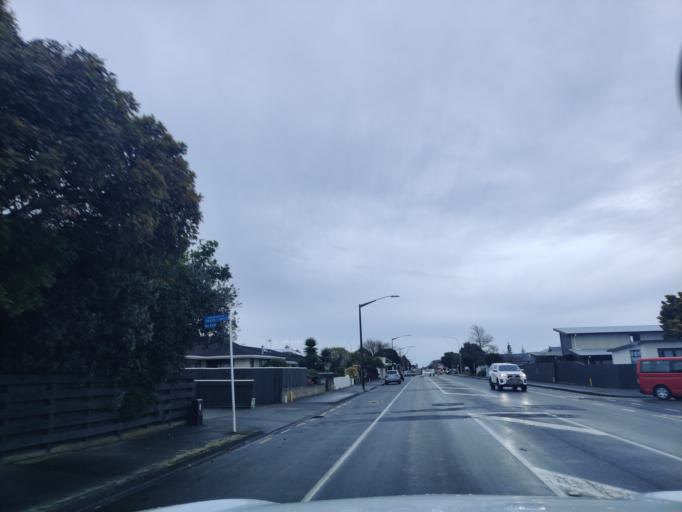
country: NZ
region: Manawatu-Wanganui
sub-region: Palmerston North City
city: Palmerston North
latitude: -40.3463
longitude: 175.6144
